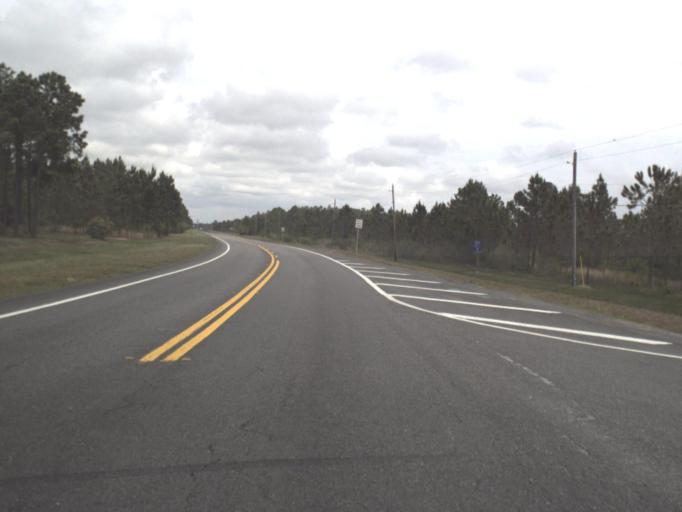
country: US
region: Florida
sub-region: Santa Rosa County
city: Tiger Point
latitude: 30.4784
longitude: -87.0792
